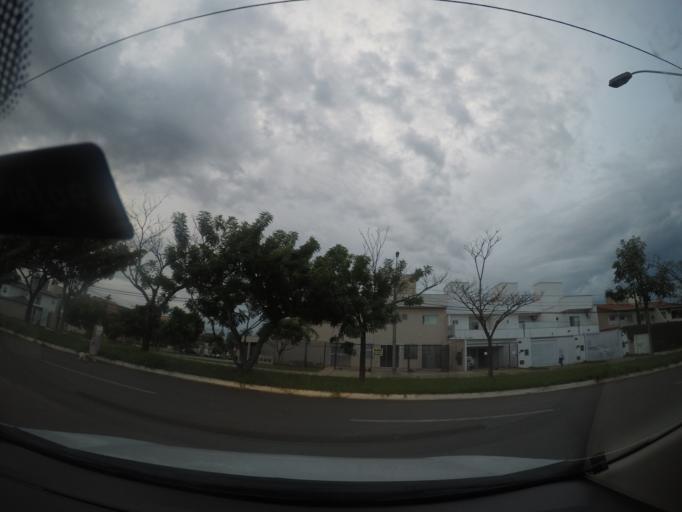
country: BR
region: Goias
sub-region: Goiania
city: Goiania
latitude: -16.6461
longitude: -49.2283
